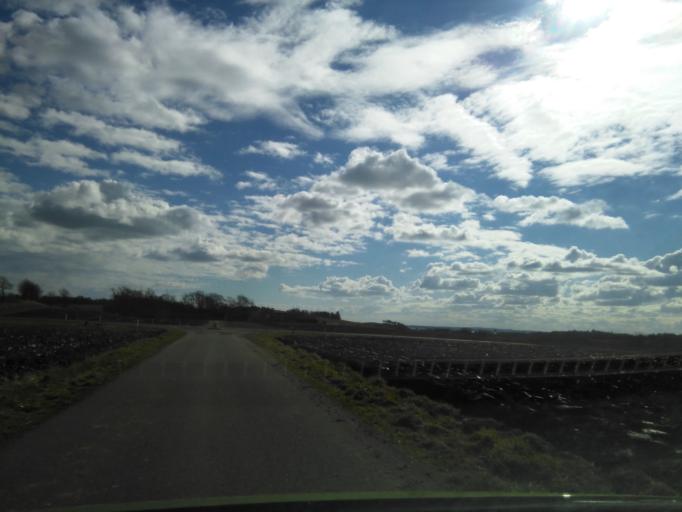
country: DK
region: Central Jutland
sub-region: Odder Kommune
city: Odder
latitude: 55.9110
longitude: 10.0364
